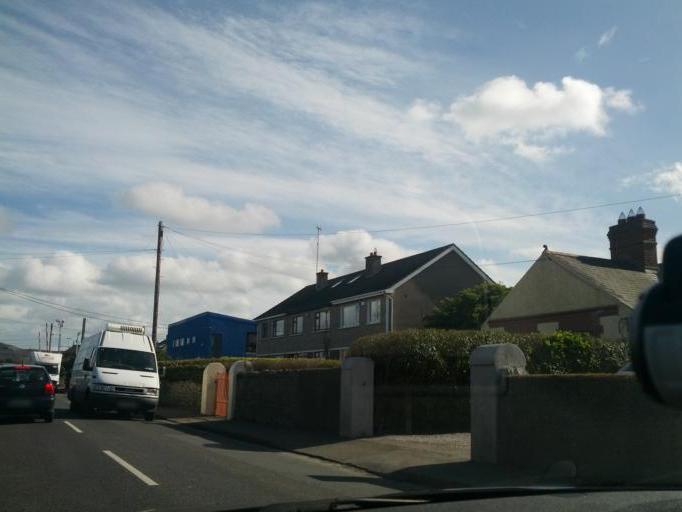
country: IE
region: Leinster
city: Sutton
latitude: 53.3927
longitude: -6.1187
